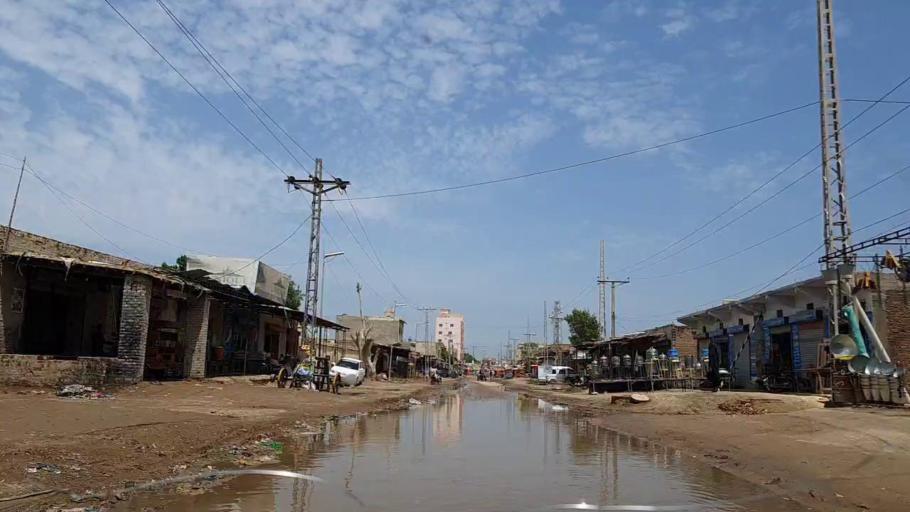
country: PK
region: Sindh
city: Naushahro Firoz
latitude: 26.8425
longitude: 68.1153
